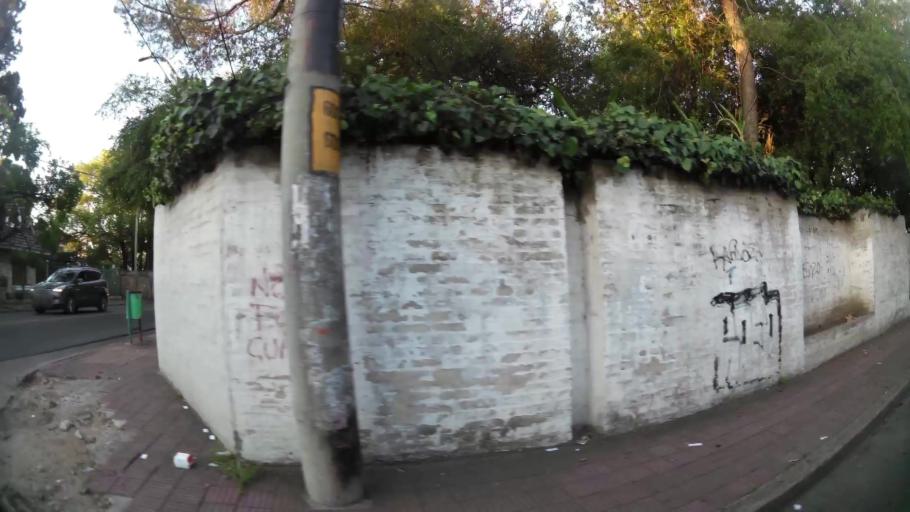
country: AR
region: Cordoba
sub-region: Departamento de Capital
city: Cordoba
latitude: -31.3783
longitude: -64.2232
